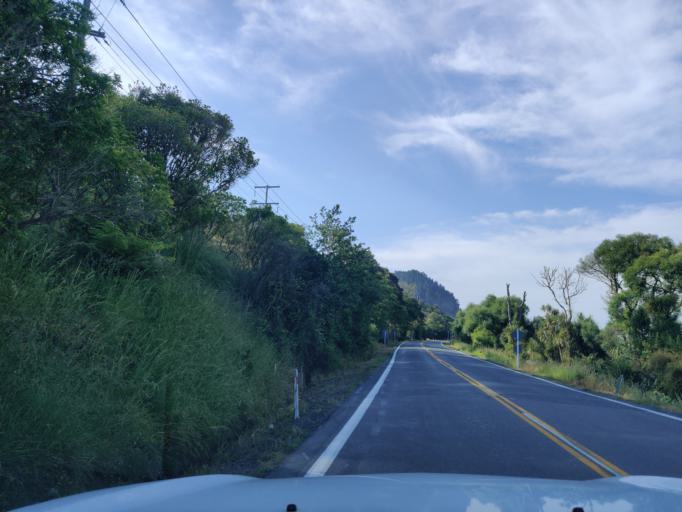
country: NZ
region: Waikato
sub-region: Waikato District
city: Ngaruawahia
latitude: -37.5975
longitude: 175.1566
